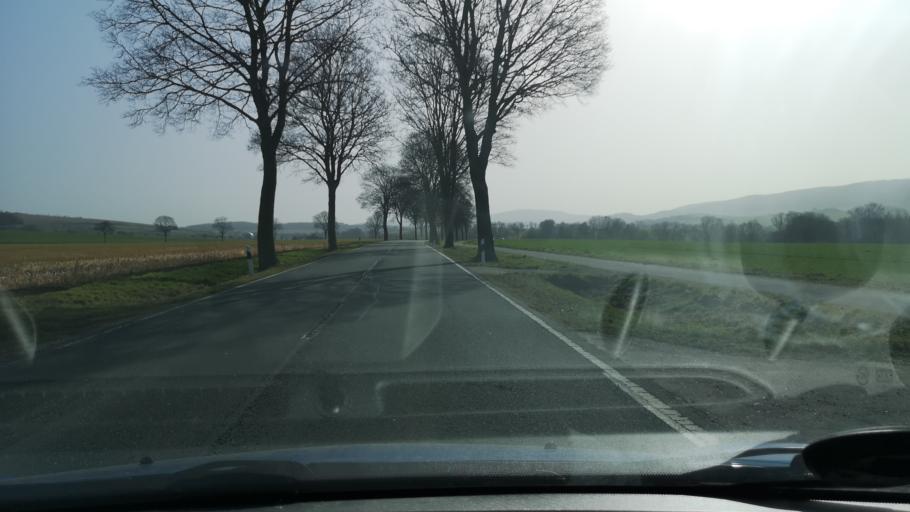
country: DE
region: Lower Saxony
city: Salzhemmendorf
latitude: 52.0414
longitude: 9.6013
